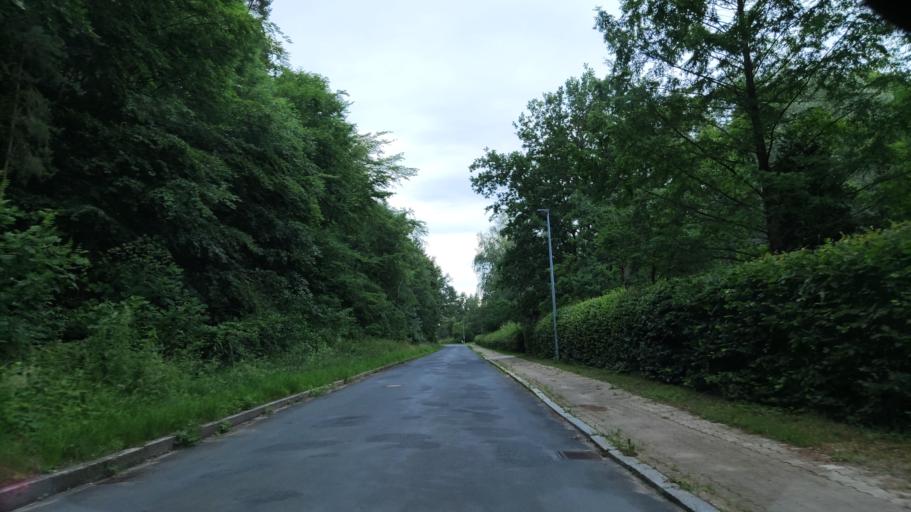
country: DE
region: Lower Saxony
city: Tosterglope
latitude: 53.2621
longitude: 10.8114
